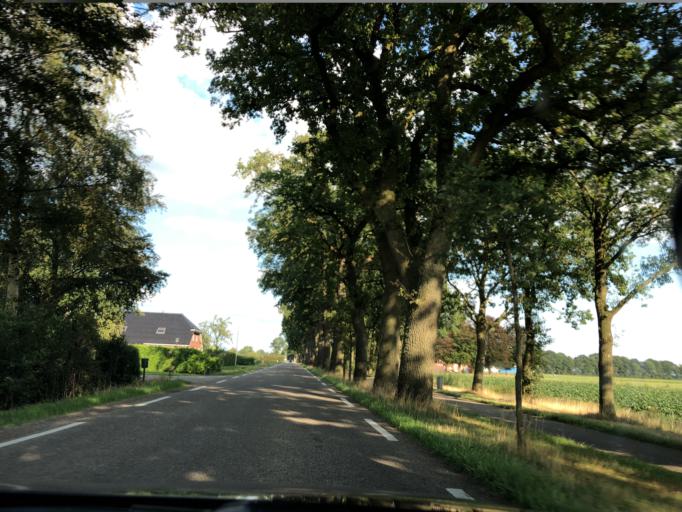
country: NL
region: Groningen
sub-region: Gemeente Vlagtwedde
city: Vlagtwedde
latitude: 53.0244
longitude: 7.1307
